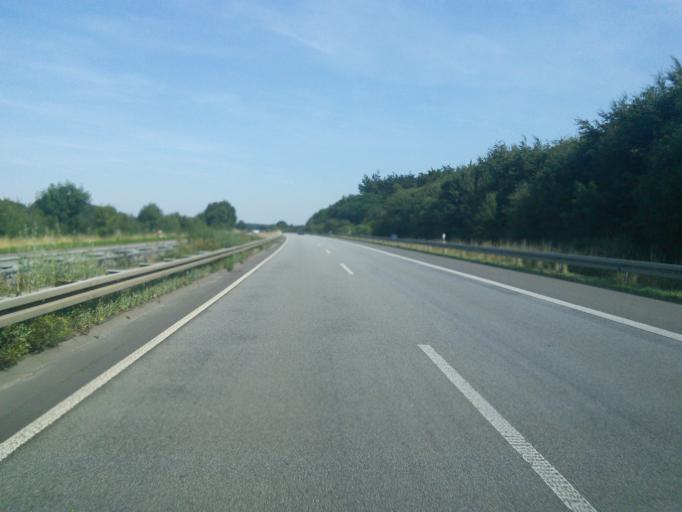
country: DE
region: North Rhine-Westphalia
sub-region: Regierungsbezirk Dusseldorf
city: Schwalmtal
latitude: 51.2001
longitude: 6.2733
